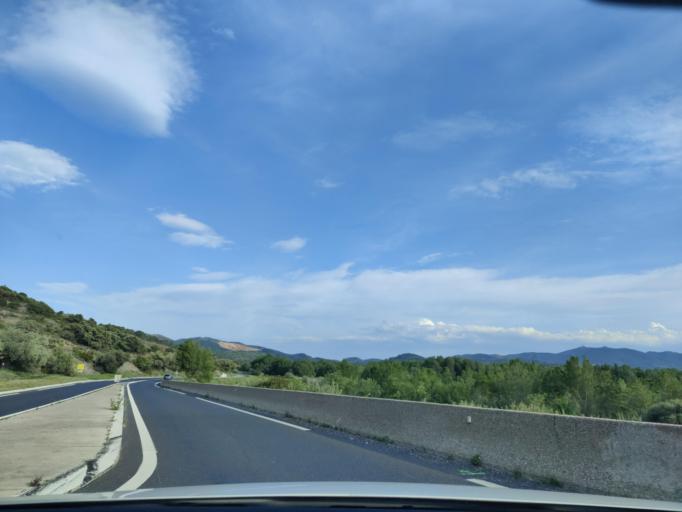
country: FR
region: Languedoc-Roussillon
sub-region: Departement des Pyrenees-Orientales
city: Estagel
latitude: 42.7846
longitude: 2.6845
